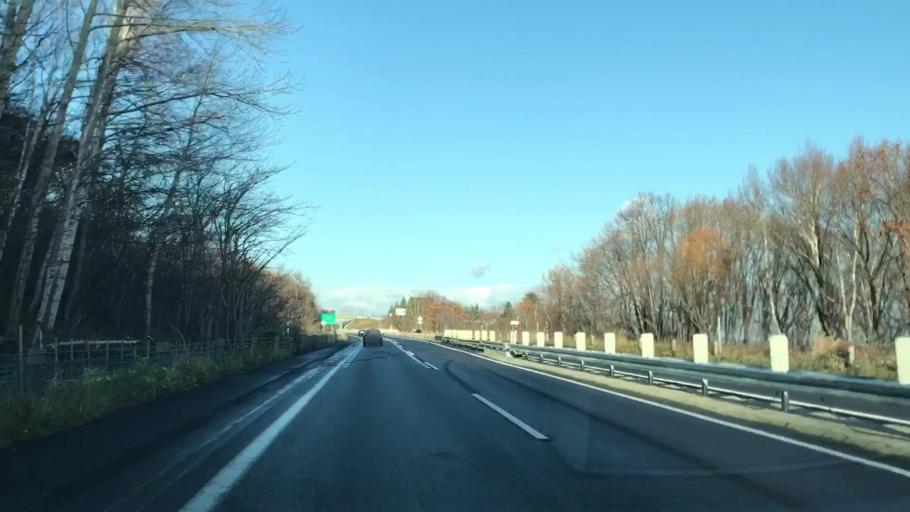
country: JP
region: Hokkaido
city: Sapporo
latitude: 43.1305
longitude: 141.1844
